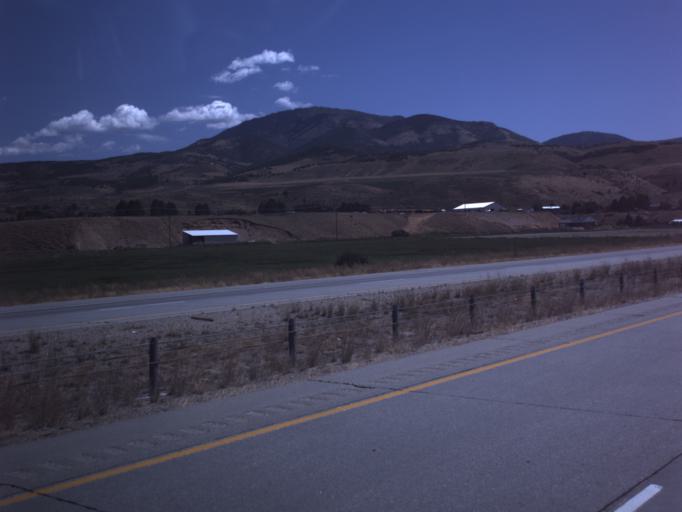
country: US
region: Utah
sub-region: Morgan County
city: Mountain Green
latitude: 41.1338
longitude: -111.7824
